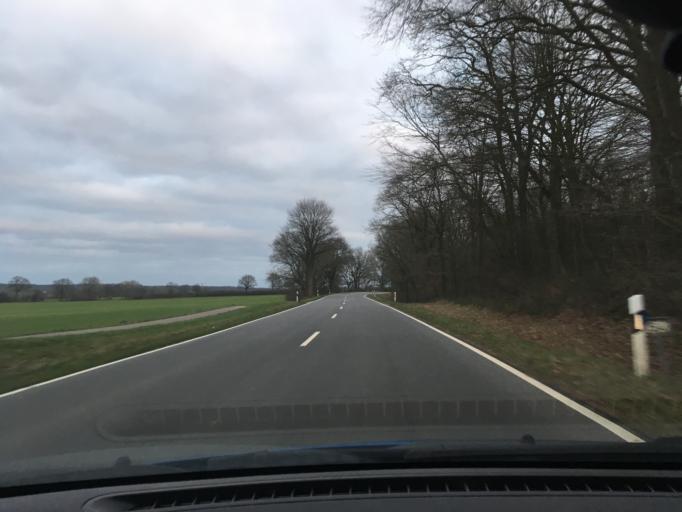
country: DE
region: Schleswig-Holstein
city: Mehlbek
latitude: 53.9961
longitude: 9.4481
